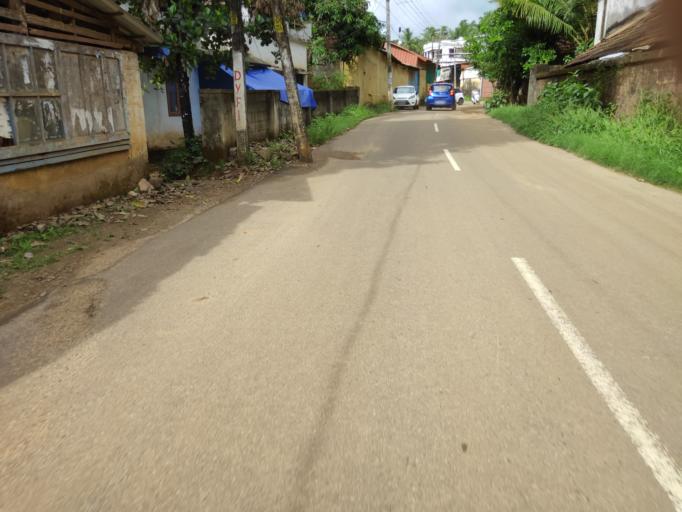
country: IN
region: Kerala
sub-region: Malappuram
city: Manjeri
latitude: 11.1336
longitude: 76.1260
